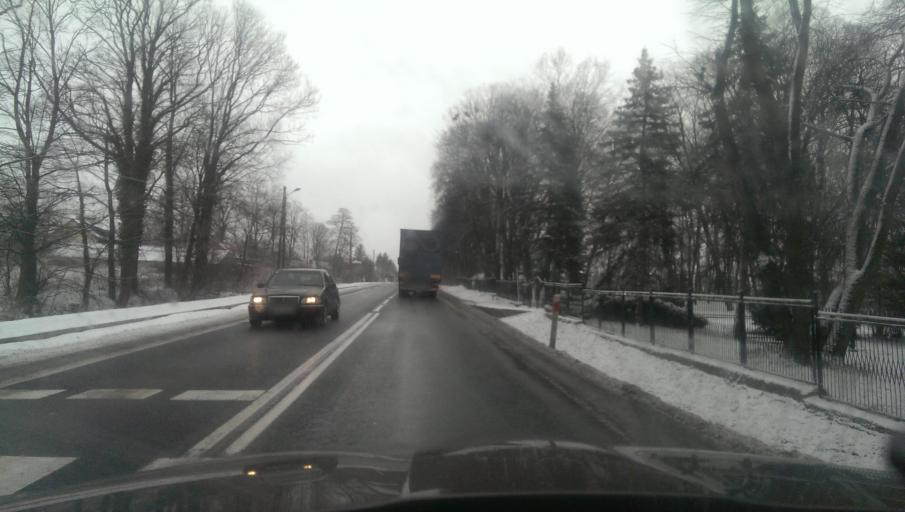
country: PL
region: Subcarpathian Voivodeship
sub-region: Powiat sanocki
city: Nowosielce-Gniewosz
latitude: 49.5640
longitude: 22.0792
